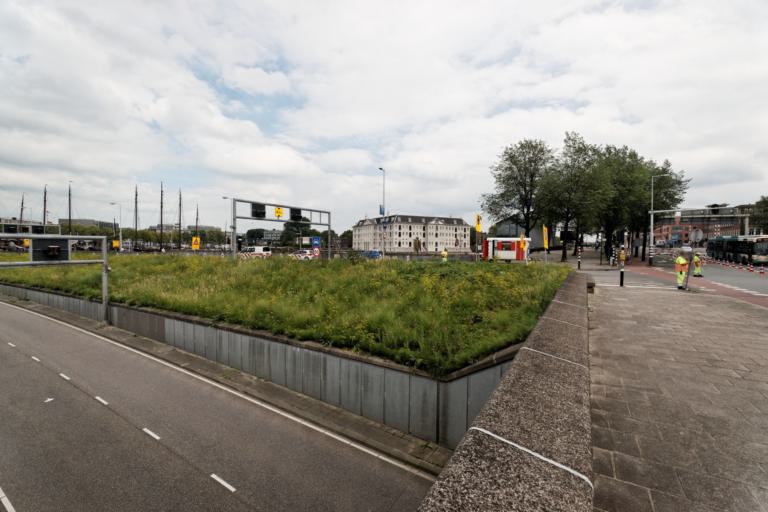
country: NL
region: North Holland
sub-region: Gemeente Amsterdam
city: Amsterdam
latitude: 52.3718
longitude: 4.9112
